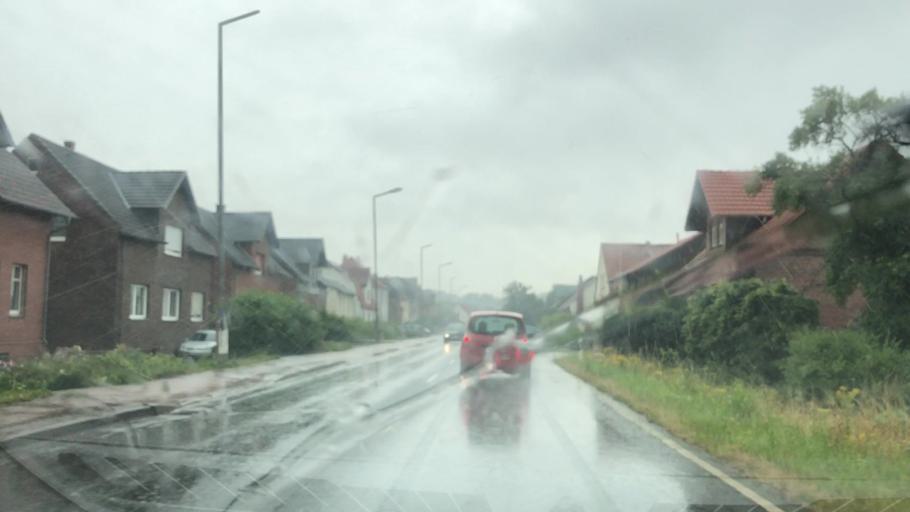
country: DE
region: North Rhine-Westphalia
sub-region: Regierungsbezirk Detmold
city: Minden
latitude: 52.2721
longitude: 8.9716
